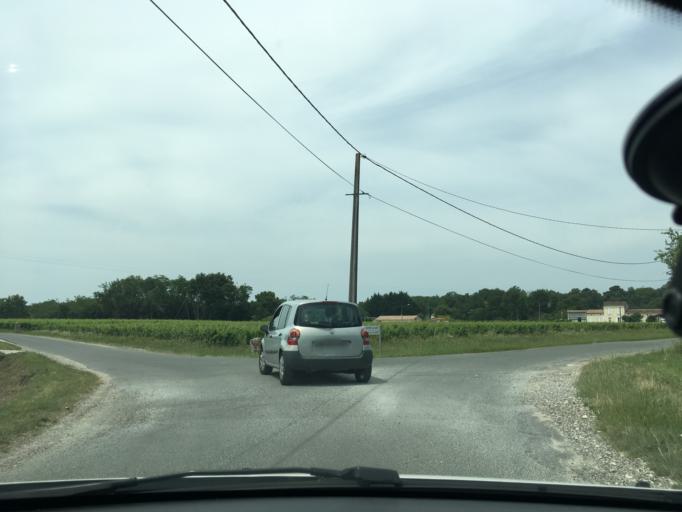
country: FR
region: Aquitaine
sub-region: Departement de la Gironde
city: Listrac-Medoc
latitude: 45.0627
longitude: -0.8010
